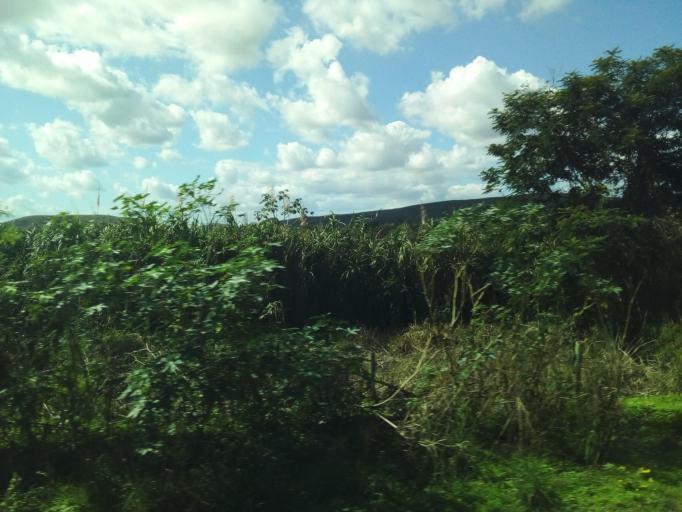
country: BR
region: Minas Gerais
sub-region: Governador Valadares
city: Governador Valadares
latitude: -18.8686
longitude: -41.7733
